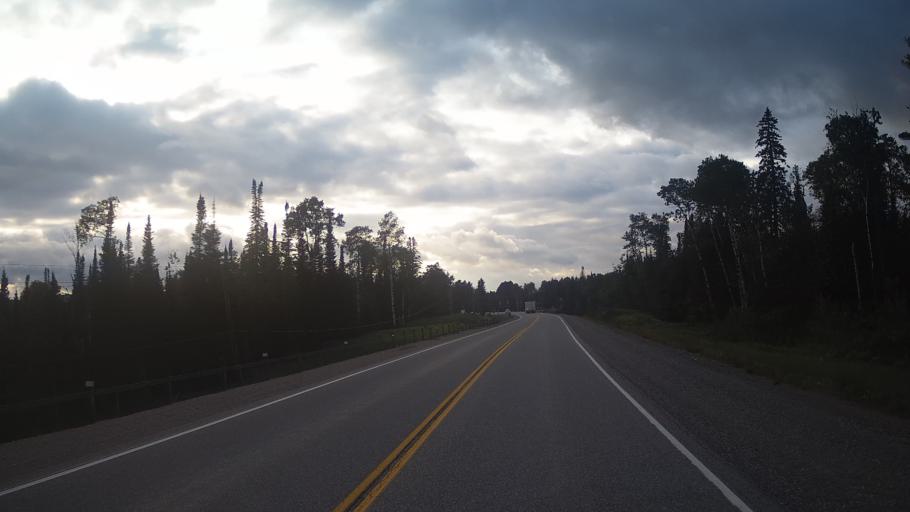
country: CA
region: Ontario
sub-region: Rainy River District
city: Atikokan
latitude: 49.0184
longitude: -90.4387
